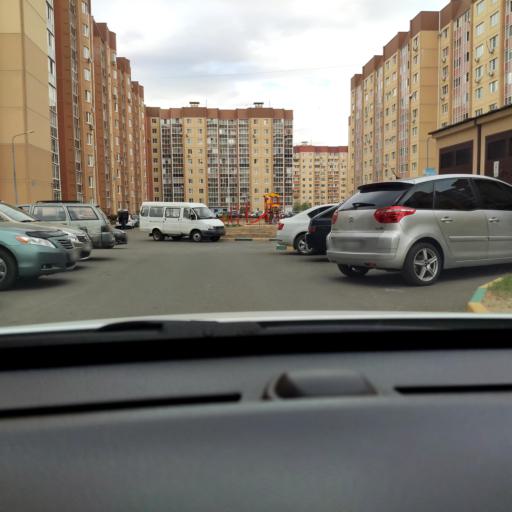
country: RU
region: Voronezj
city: Voronezh
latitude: 51.7166
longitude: 39.2636
